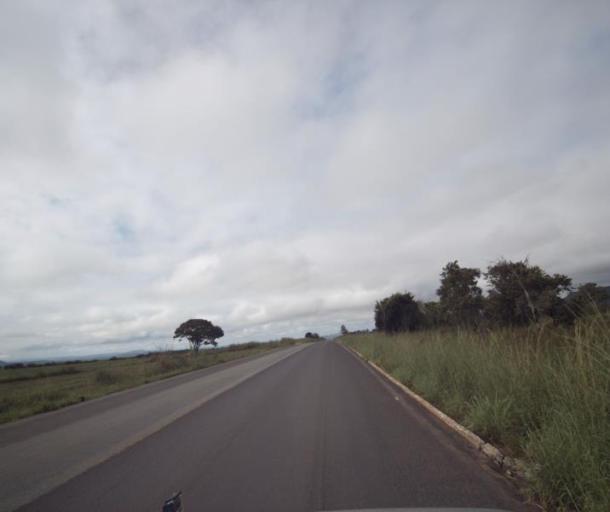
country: BR
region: Goias
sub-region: Padre Bernardo
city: Padre Bernardo
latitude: -15.3558
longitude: -48.6466
